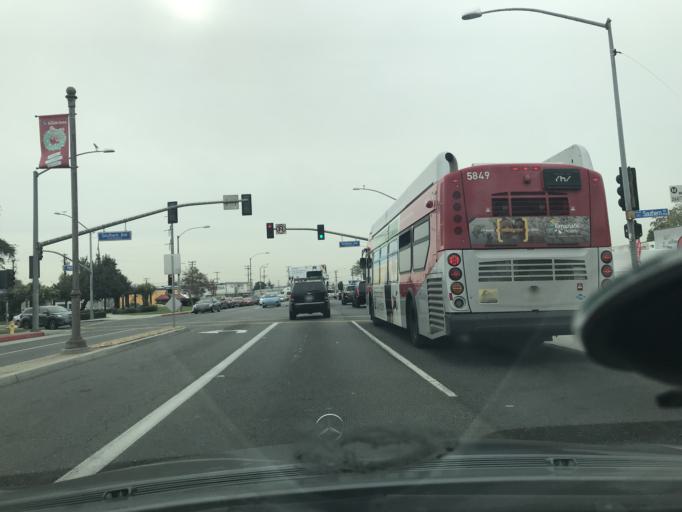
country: US
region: California
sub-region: Los Angeles County
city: Cudahy
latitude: 33.9466
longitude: -118.1812
